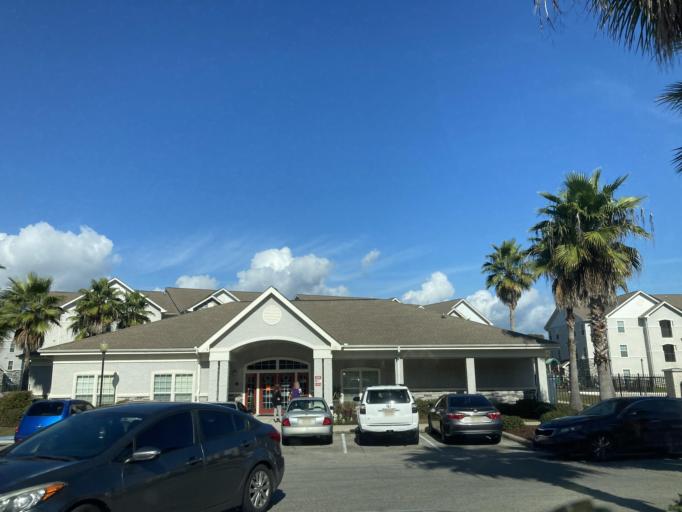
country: US
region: Mississippi
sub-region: Harrison County
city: Gulfport
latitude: 30.3843
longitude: -89.0790
